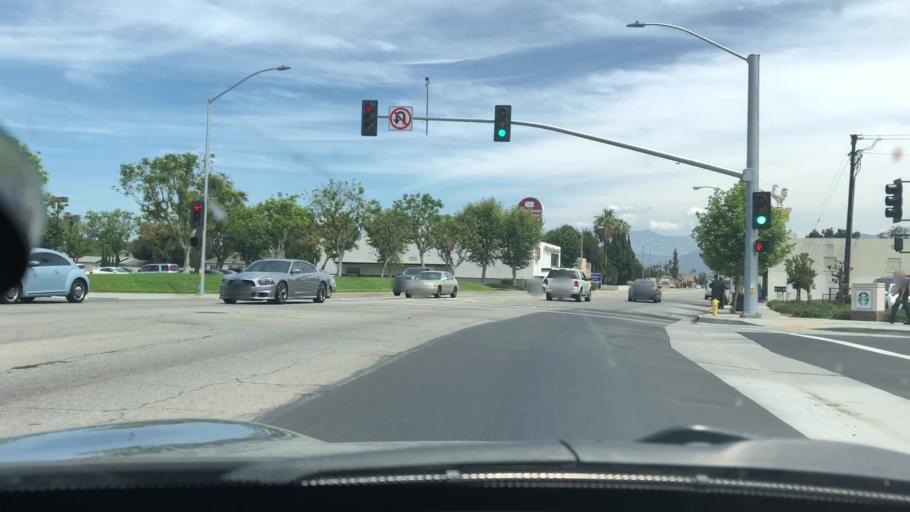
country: US
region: California
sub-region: Los Angeles County
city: Pomona
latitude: 34.0677
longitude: -117.7519
